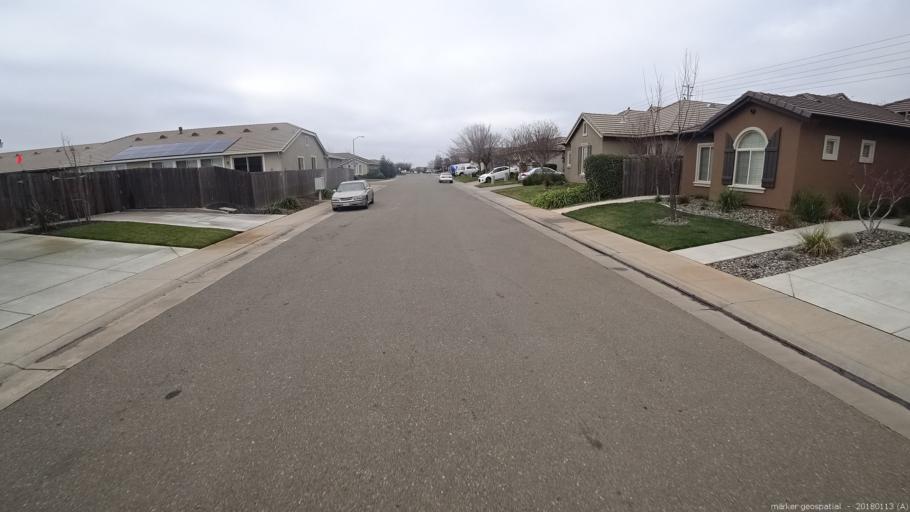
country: US
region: California
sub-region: Sacramento County
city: Gold River
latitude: 38.5587
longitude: -121.2092
